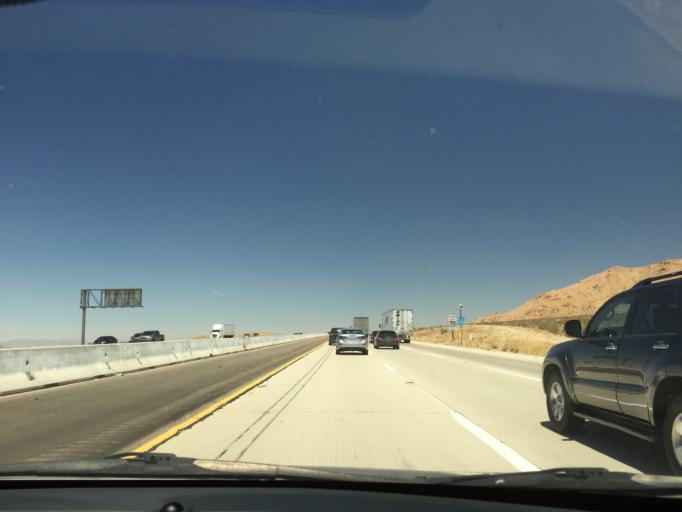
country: US
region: California
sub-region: San Bernardino County
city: Lenwood
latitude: 34.7148
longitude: -117.1982
